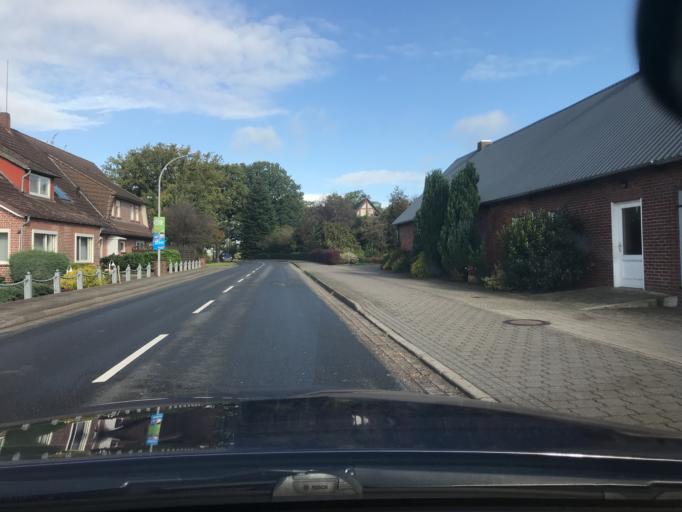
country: DE
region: Lower Saxony
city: Ahlerstedt
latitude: 53.3789
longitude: 9.4649
